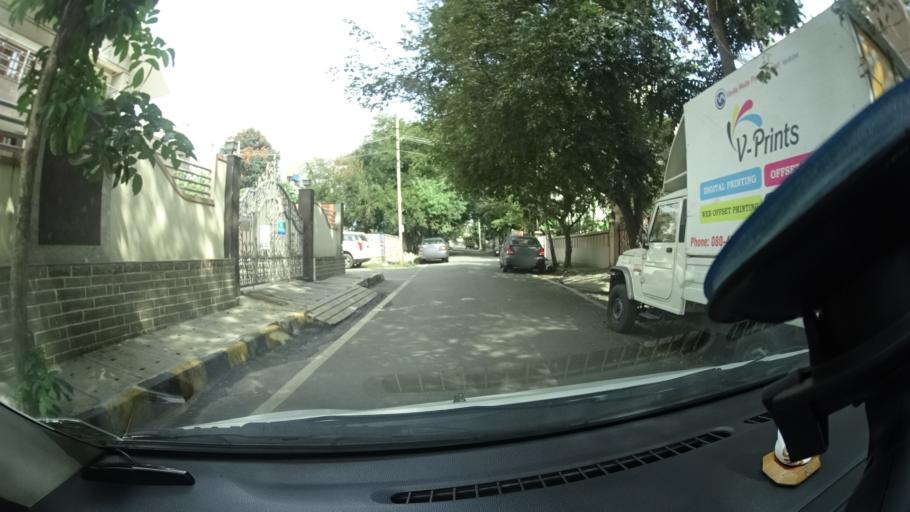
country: IN
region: Karnataka
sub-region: Bangalore Urban
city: Yelahanka
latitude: 13.0975
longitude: 77.5849
